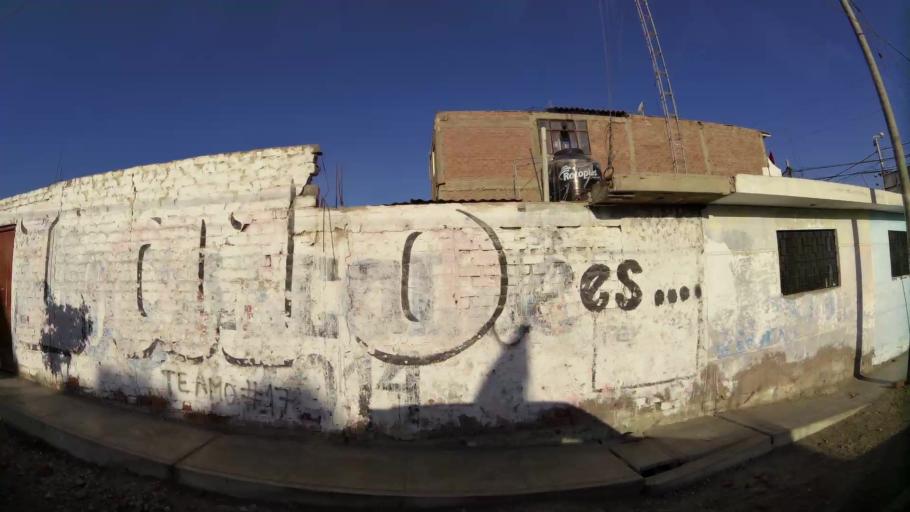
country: PE
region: Ica
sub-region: Provincia de Pisco
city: Villa Tupac Amaru
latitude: -13.7127
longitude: -76.1488
